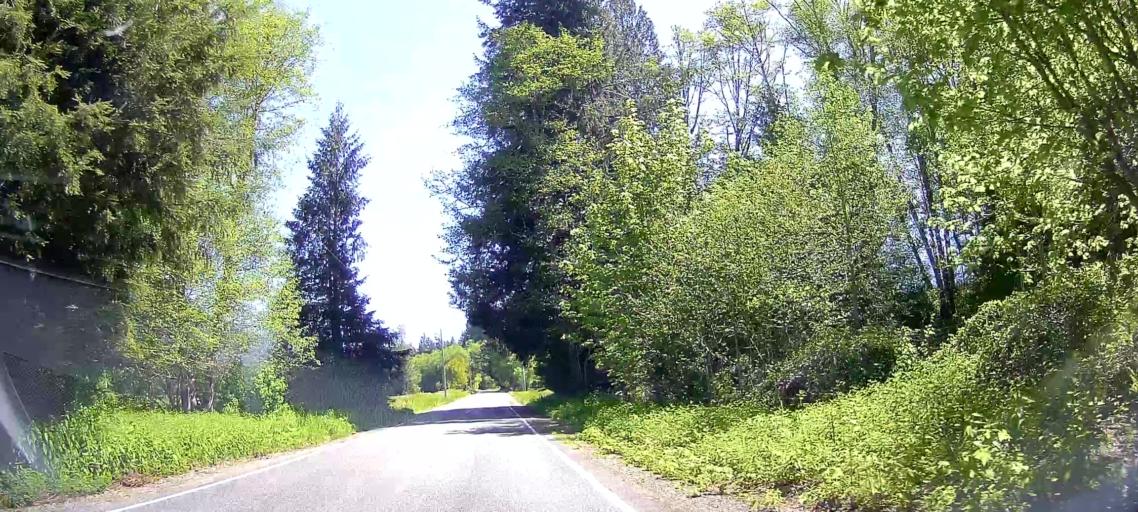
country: US
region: Washington
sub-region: Snohomish County
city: Darrington
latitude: 48.4729
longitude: -121.6365
